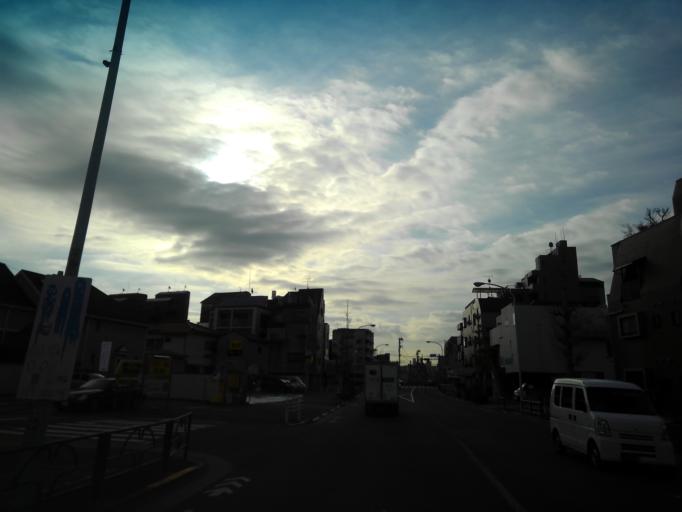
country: JP
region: Tokyo
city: Tokyo
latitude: 35.6696
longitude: 139.6725
